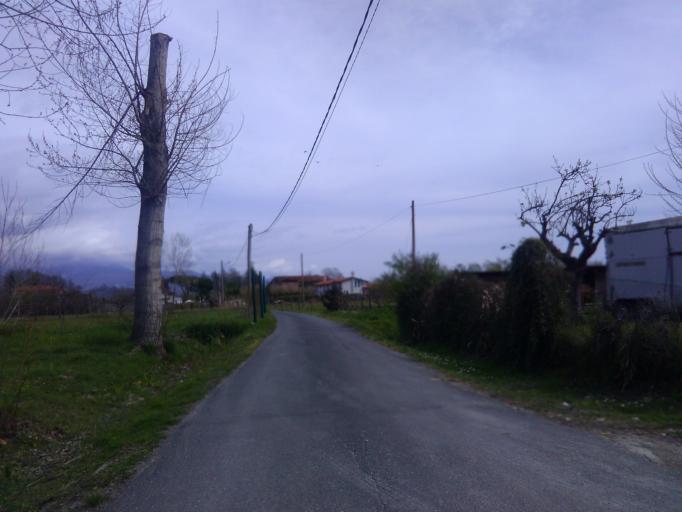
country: IT
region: Liguria
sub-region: Provincia di La Spezia
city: Casano-Dogana-Isola
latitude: 44.0558
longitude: 10.0292
